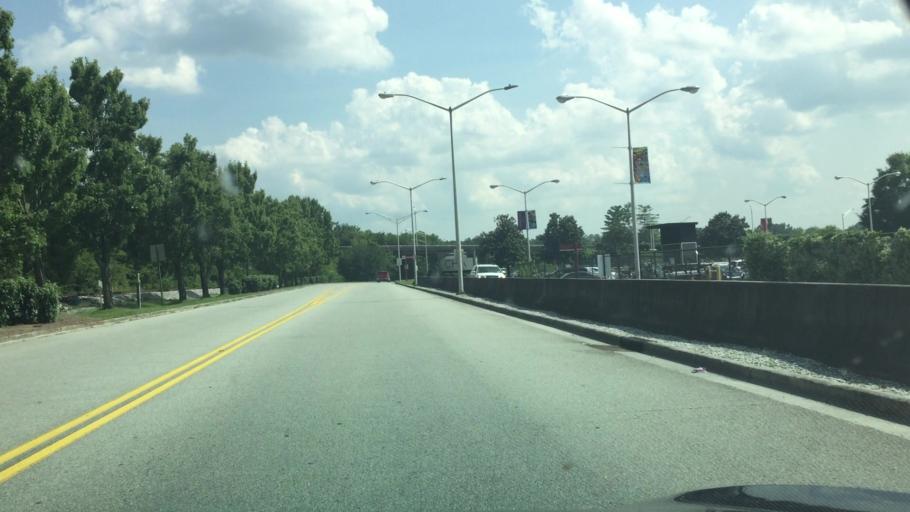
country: US
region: Tennessee
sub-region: Hamilton County
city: East Brainerd
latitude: 35.0363
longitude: -85.1949
